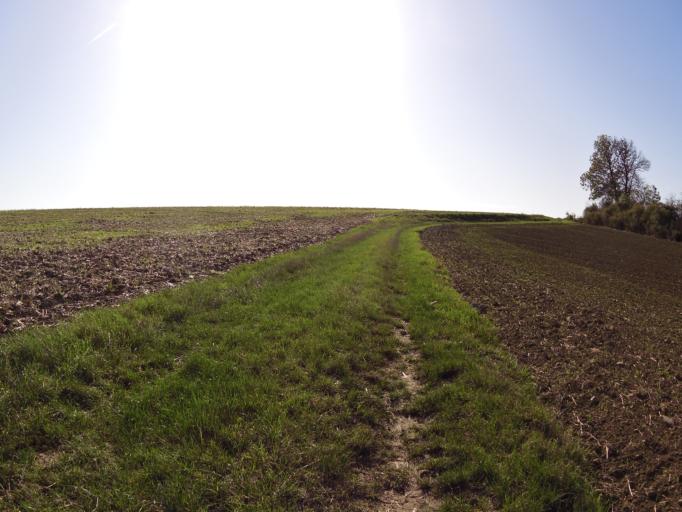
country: DE
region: Bavaria
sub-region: Regierungsbezirk Unterfranken
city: Theilheim
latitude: 49.7526
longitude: 10.0596
